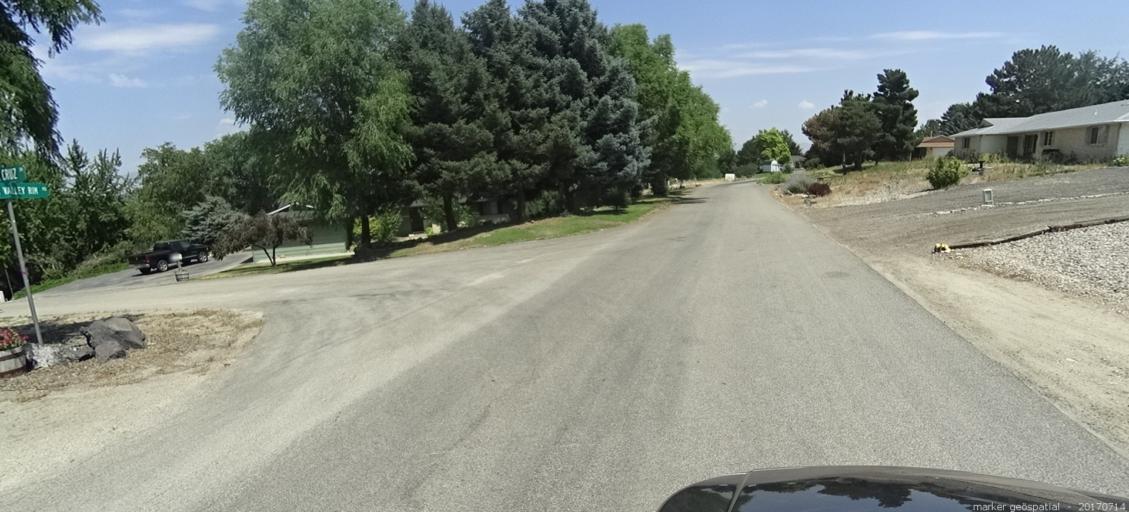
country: US
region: Idaho
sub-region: Ada County
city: Meridian
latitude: 43.5392
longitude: -116.3307
